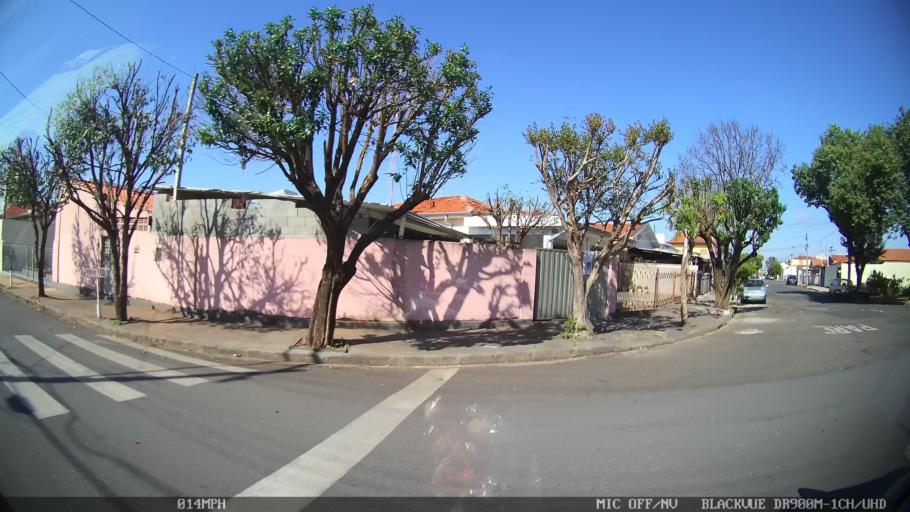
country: BR
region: Sao Paulo
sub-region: Americana
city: Americana
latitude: -22.7560
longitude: -47.3352
